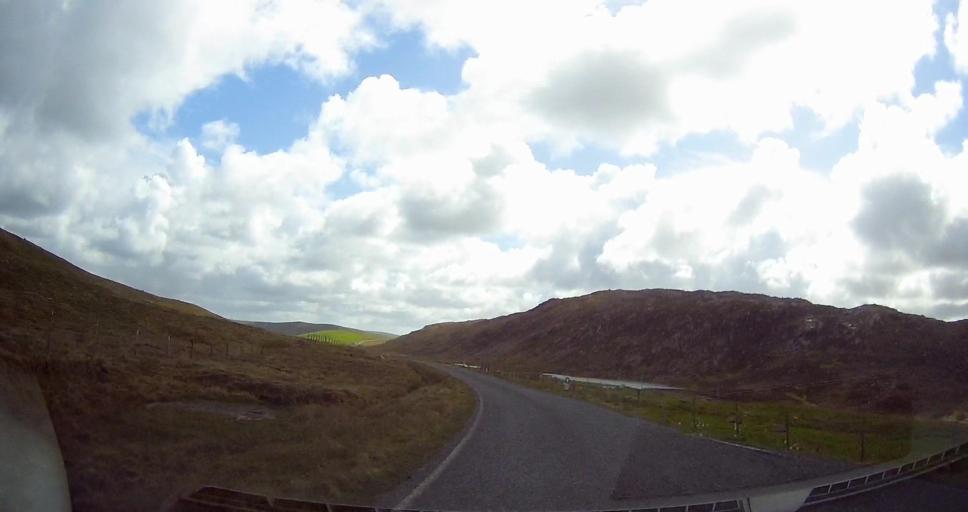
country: GB
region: Scotland
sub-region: Shetland Islands
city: Lerwick
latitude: 60.5572
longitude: -1.3379
